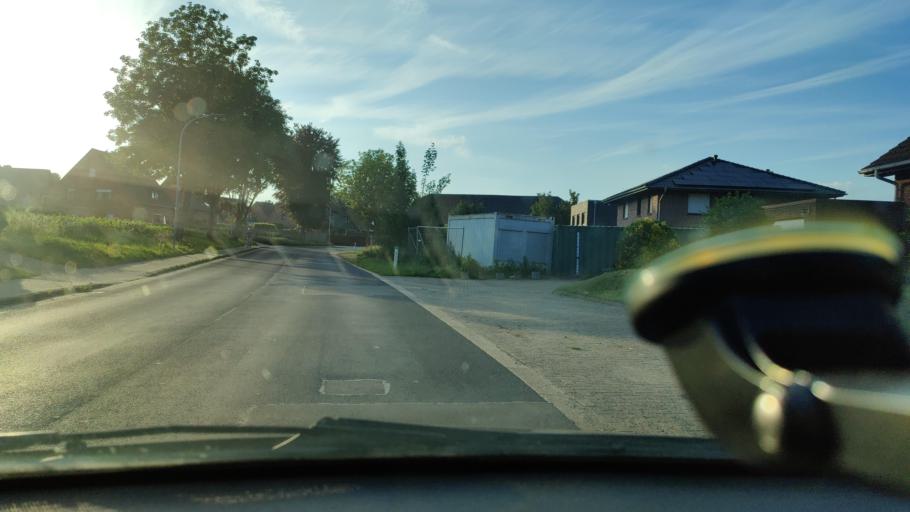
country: DE
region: North Rhine-Westphalia
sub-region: Regierungsbezirk Dusseldorf
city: Rheurdt
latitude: 51.4609
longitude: 6.4754
